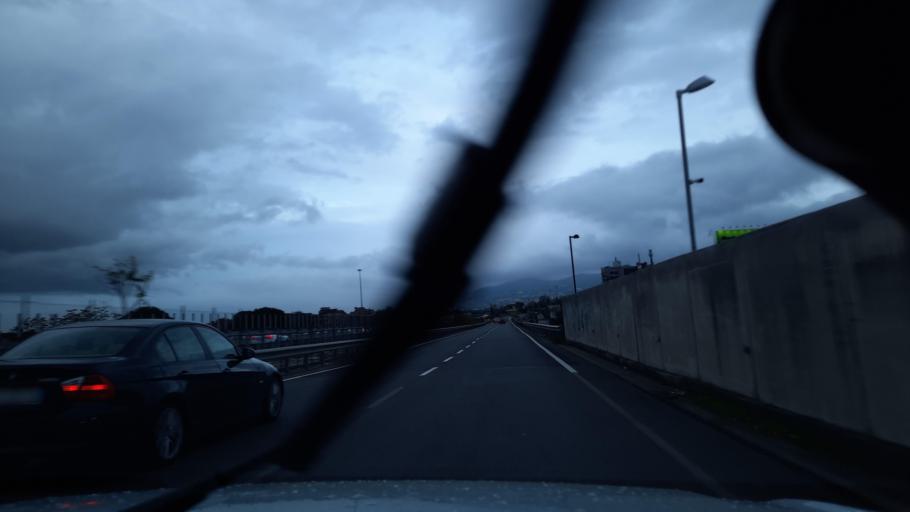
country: IT
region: Latium
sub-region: Citta metropolitana di Roma Capitale
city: Ciampino
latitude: 41.8515
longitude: 12.6013
